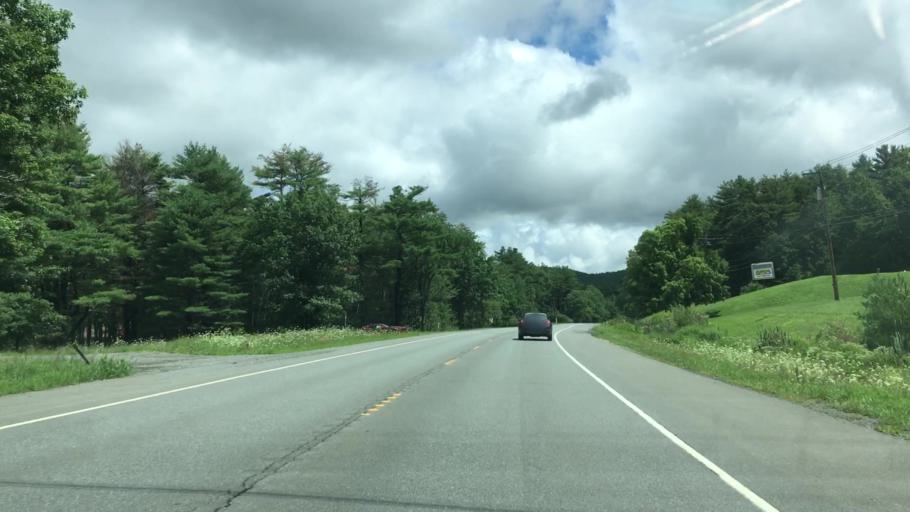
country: US
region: New York
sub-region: Rensselaer County
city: Hoosick Falls
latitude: 42.8510
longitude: -73.4278
